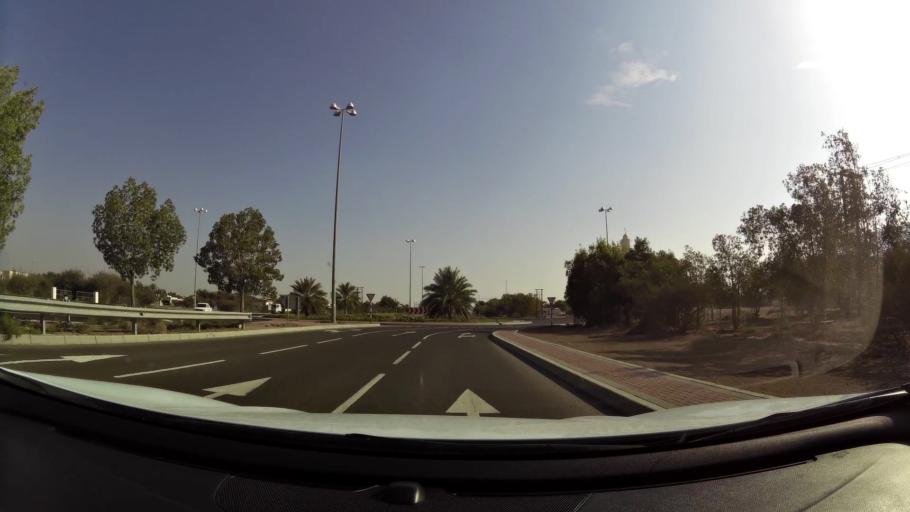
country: AE
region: Abu Dhabi
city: Al Ain
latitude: 24.0455
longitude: 55.8422
